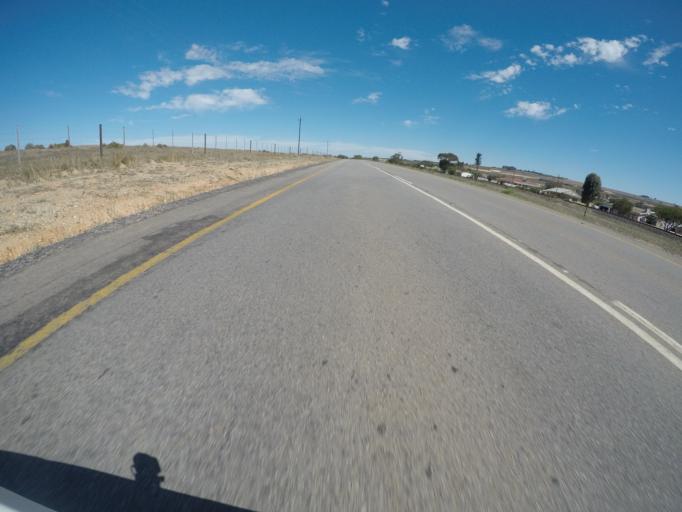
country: ZA
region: Western Cape
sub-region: West Coast District Municipality
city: Malmesbury
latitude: -33.4866
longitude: 18.6889
